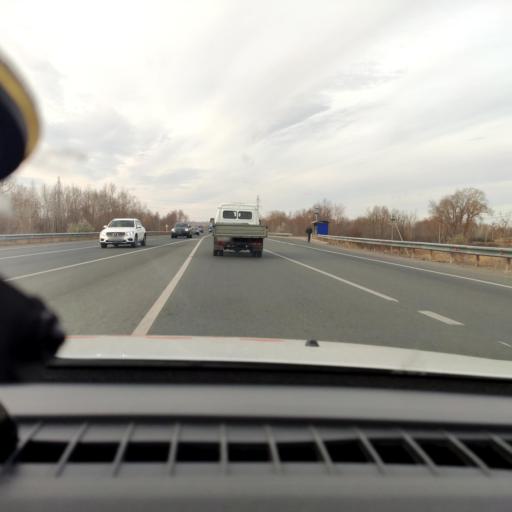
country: RU
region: Samara
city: Novokuybyshevsk
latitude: 53.1371
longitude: 49.9733
